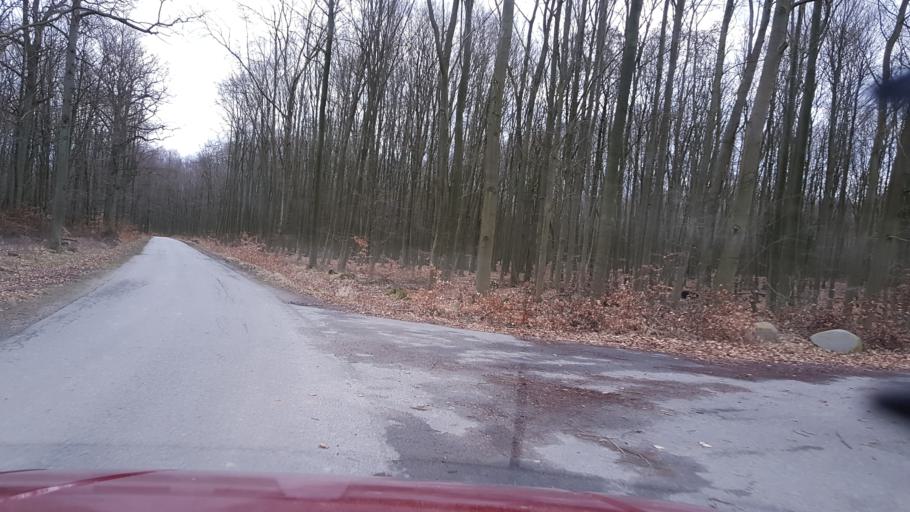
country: PL
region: West Pomeranian Voivodeship
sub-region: Powiat gryfinski
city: Stare Czarnowo
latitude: 53.3128
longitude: 14.7196
